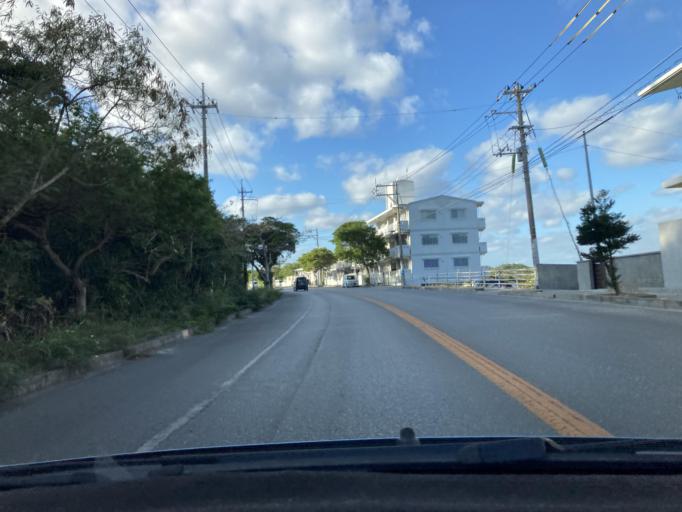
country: JP
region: Okinawa
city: Katsuren-haebaru
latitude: 26.3426
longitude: 127.8784
